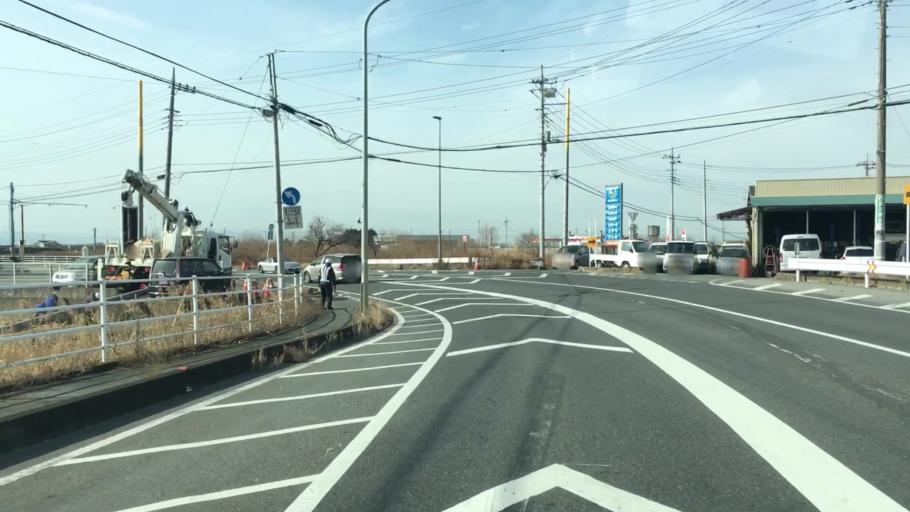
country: JP
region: Saitama
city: Menuma
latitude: 36.2450
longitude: 139.3842
